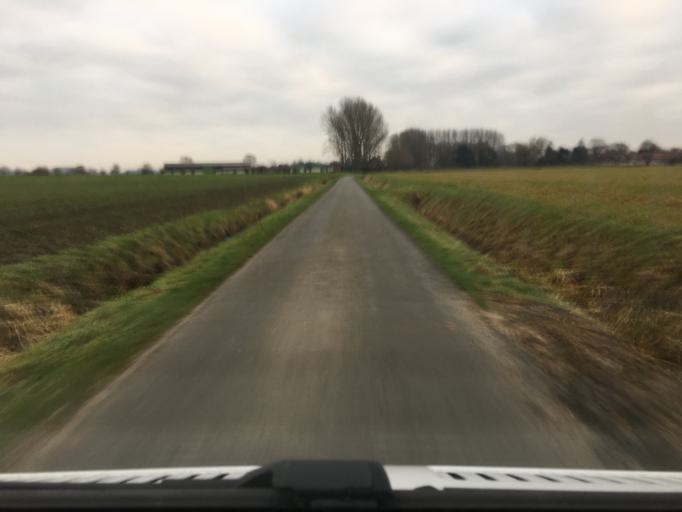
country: FR
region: Nord-Pas-de-Calais
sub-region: Departement du Nord
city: Comines
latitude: 50.7474
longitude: 3.0179
